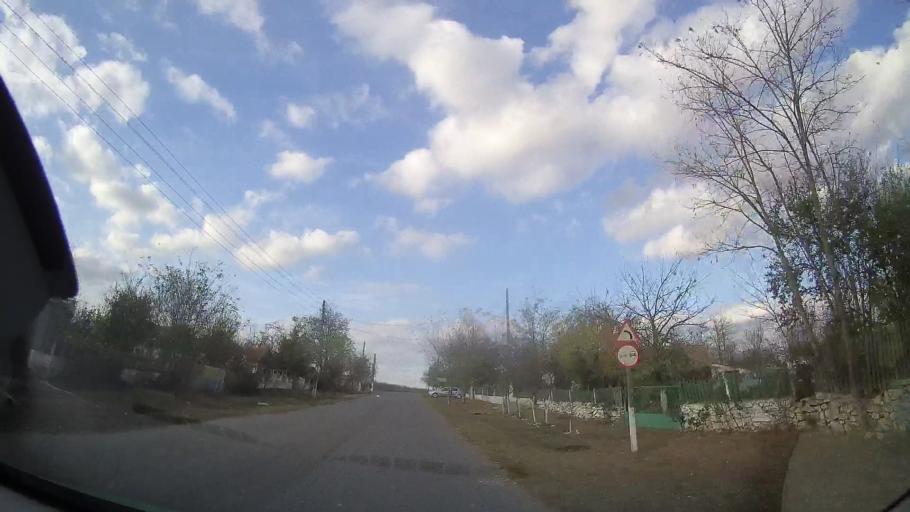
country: RO
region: Constanta
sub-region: Comuna Cerchezu
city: Cerchezu
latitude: 43.8634
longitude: 28.1002
